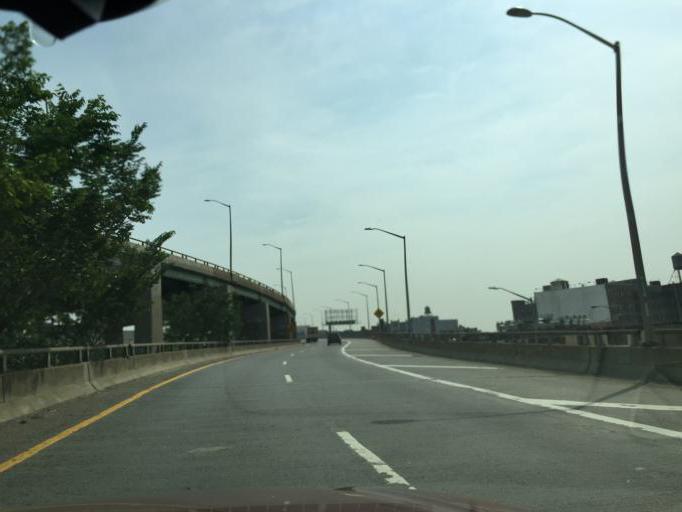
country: US
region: New York
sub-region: New York County
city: Manhattan
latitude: 40.8031
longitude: -73.9154
